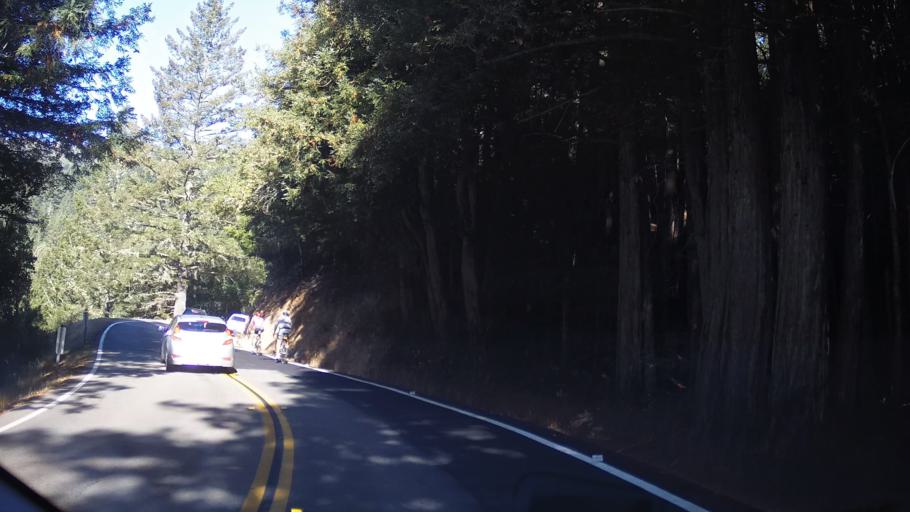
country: US
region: California
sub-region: Marin County
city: Mill Valley
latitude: 37.9127
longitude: -122.5807
